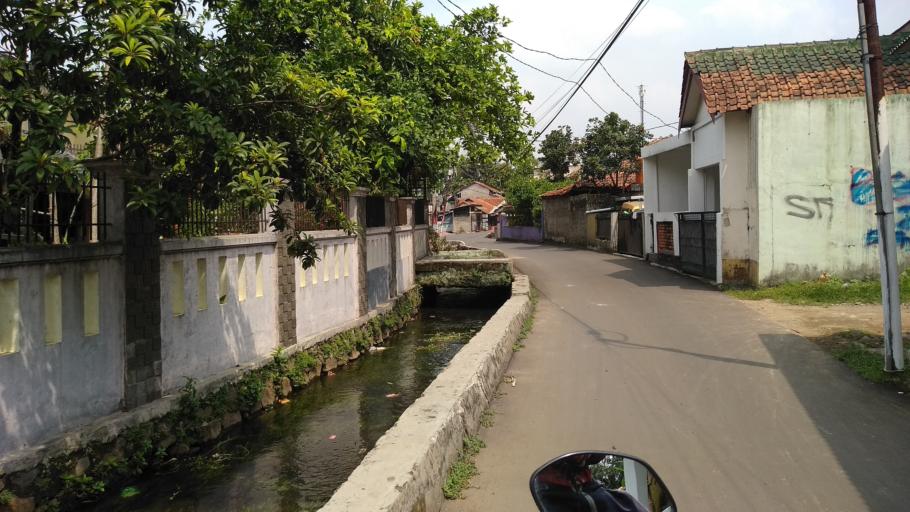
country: ID
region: West Java
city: Ciampea
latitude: -6.5557
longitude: 106.7454
